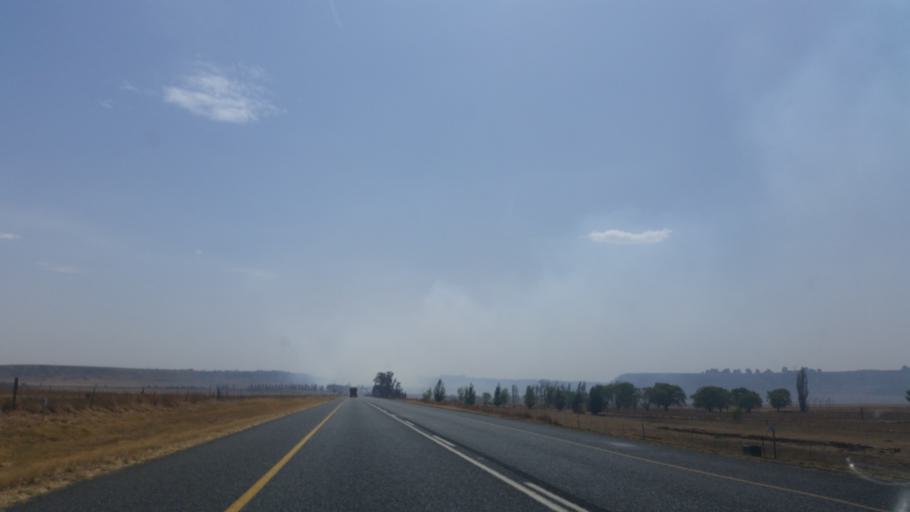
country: ZA
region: Orange Free State
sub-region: Thabo Mofutsanyana District Municipality
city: Bethlehem
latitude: -28.2789
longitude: 28.3855
